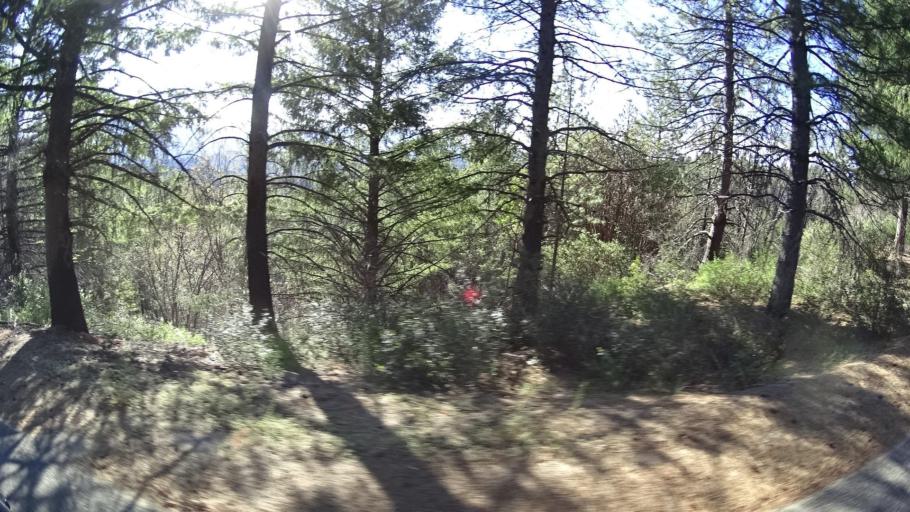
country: US
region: California
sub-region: Lake County
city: Upper Lake
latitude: 39.3167
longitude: -122.9468
